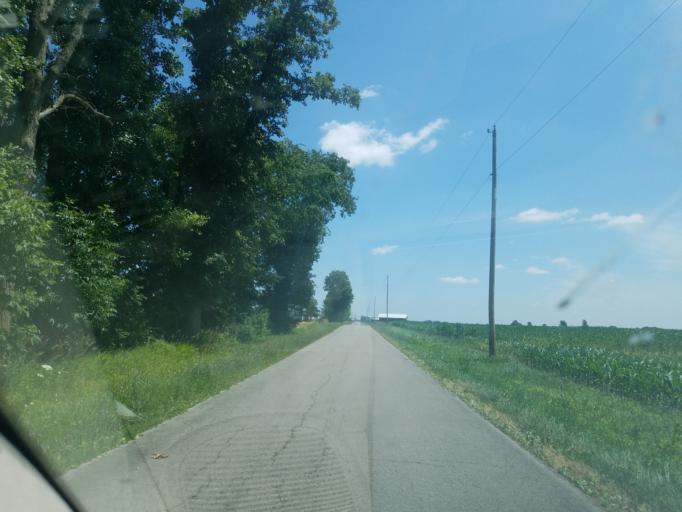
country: US
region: Ohio
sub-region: Hancock County
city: Arlington
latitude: 40.8493
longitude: -83.5958
